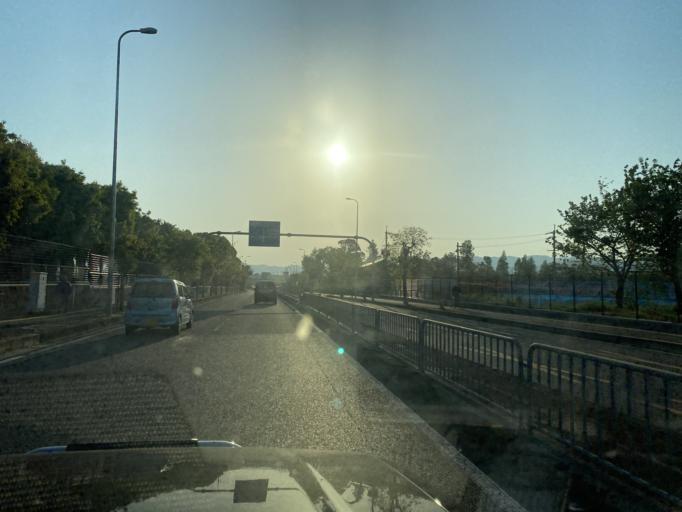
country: JP
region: Osaka
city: Ikeda
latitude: 34.8112
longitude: 135.4350
